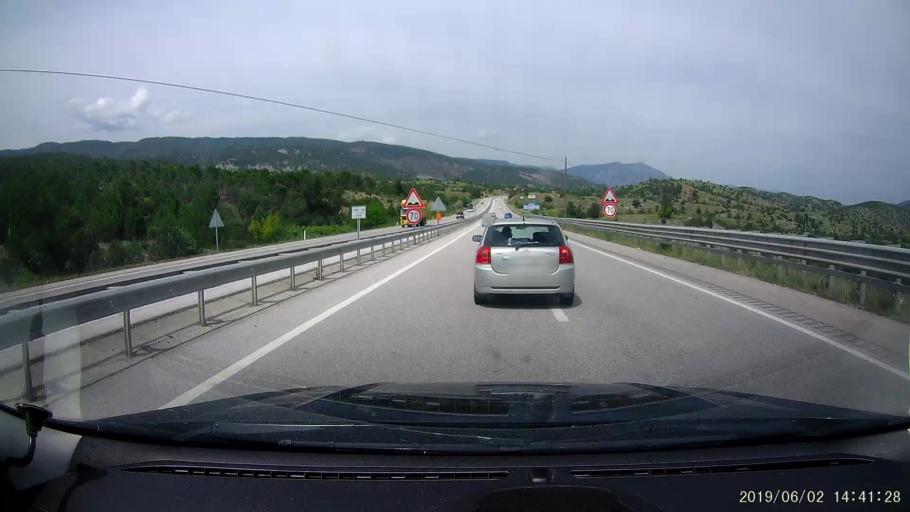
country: TR
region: Corum
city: Hacihamza
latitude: 41.0868
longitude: 34.3400
